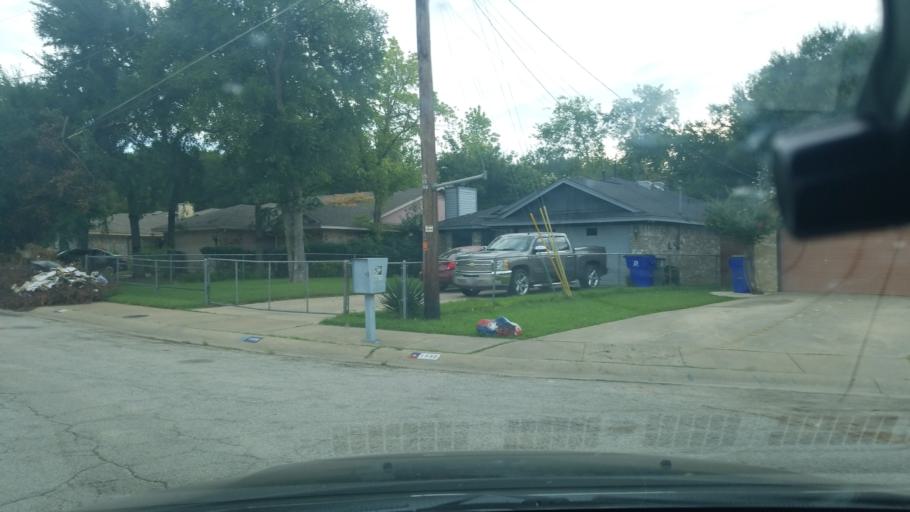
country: US
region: Texas
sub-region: Dallas County
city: Balch Springs
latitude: 32.7347
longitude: -96.6604
